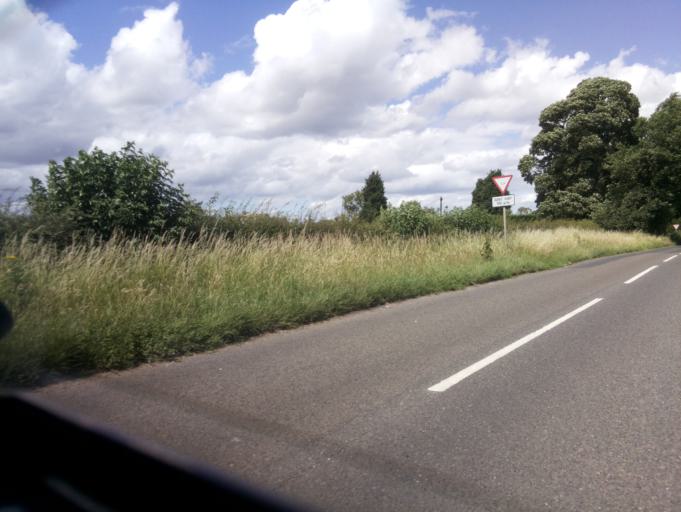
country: GB
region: England
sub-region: Nottinghamshire
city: Cotgrave
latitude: 52.9217
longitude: -1.0175
